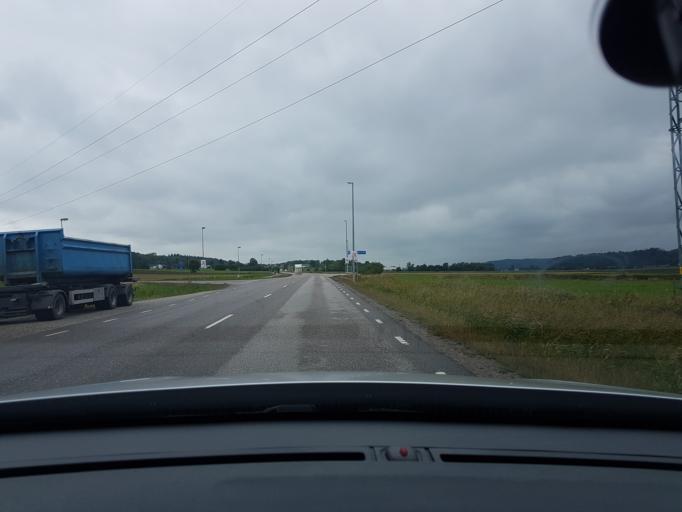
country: SE
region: Vaestra Goetaland
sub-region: Ale Kommun
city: Skepplanda
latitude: 57.9762
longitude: 12.1868
